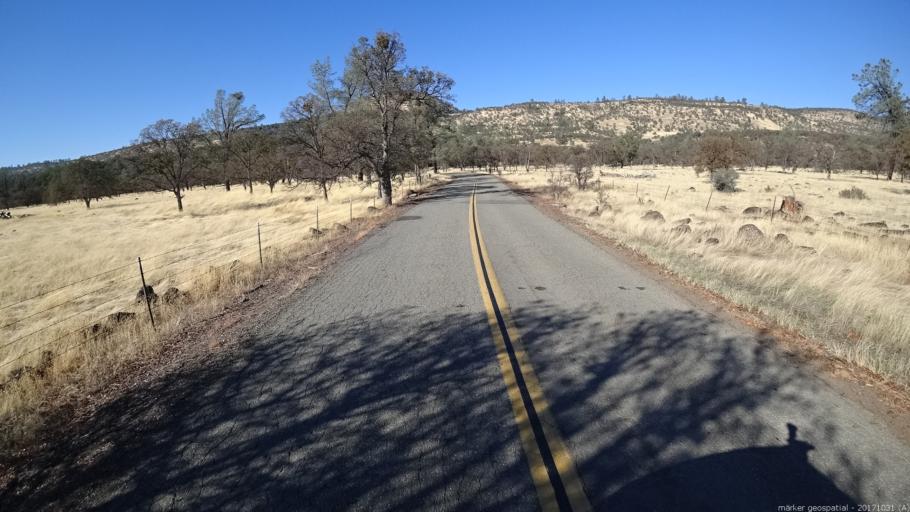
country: US
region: California
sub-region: Shasta County
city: Shingletown
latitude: 40.4372
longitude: -121.9839
